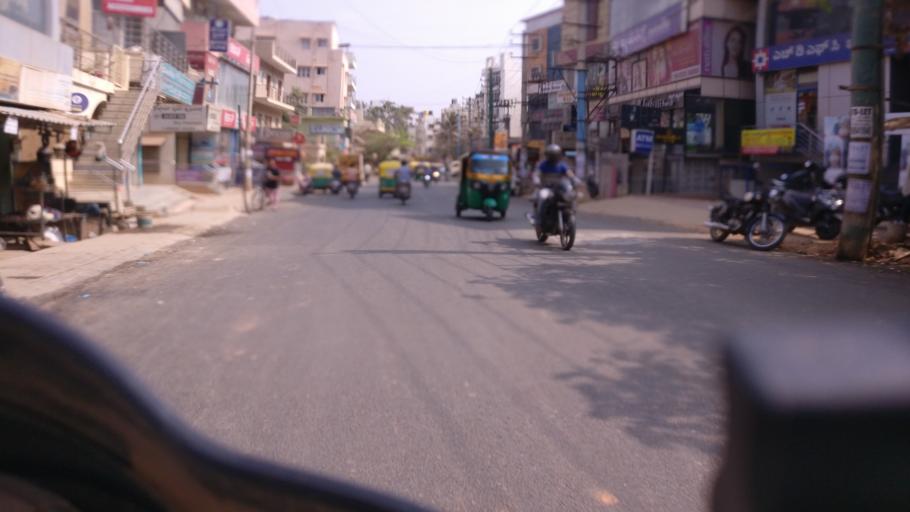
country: IN
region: Karnataka
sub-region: Bangalore Urban
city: Bangalore
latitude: 12.9077
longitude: 77.6759
